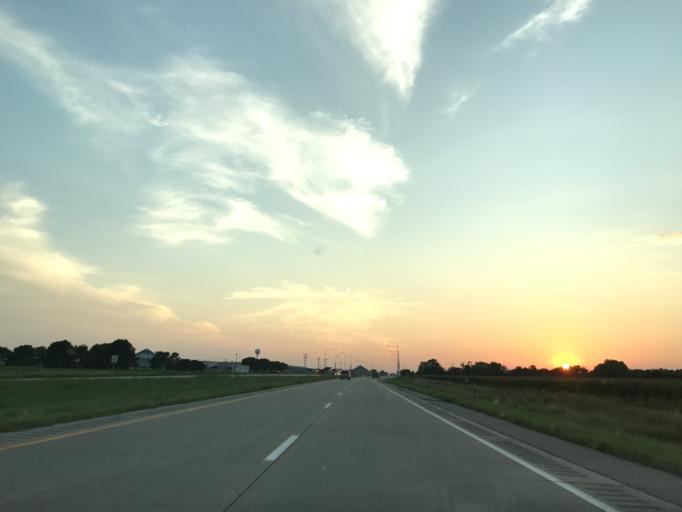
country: US
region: Nebraska
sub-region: Platte County
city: Columbus
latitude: 41.4389
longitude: -97.2678
